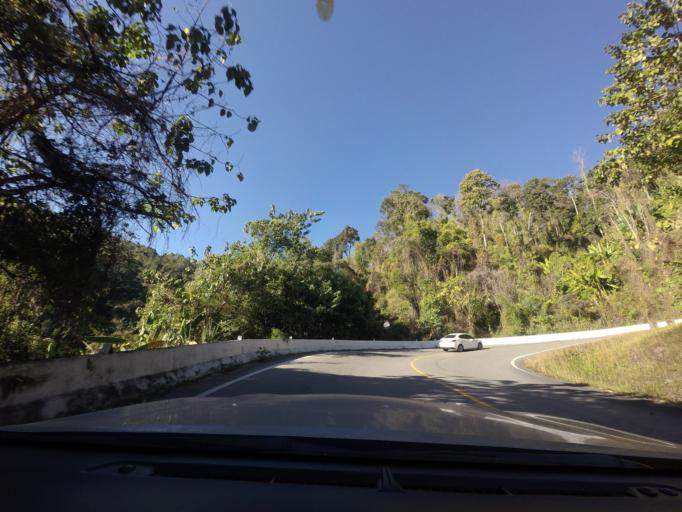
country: TH
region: Mae Hong Son
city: Mae Hi
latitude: 19.2275
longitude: 98.6705
